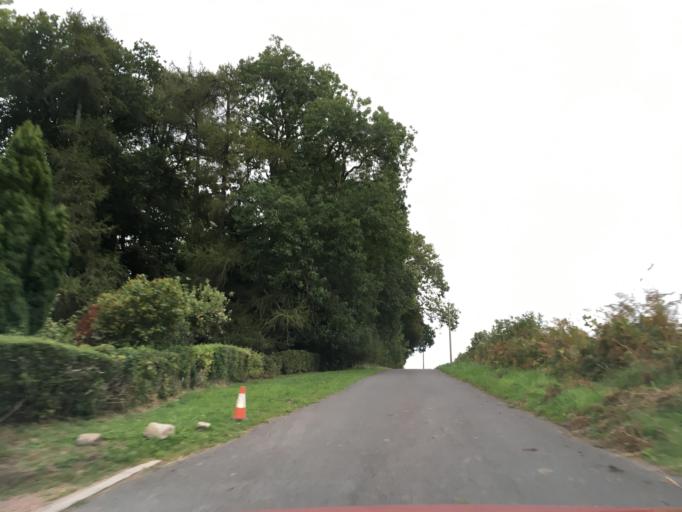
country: GB
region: Wales
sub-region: Newport
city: Caerleon
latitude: 51.6376
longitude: -2.9313
